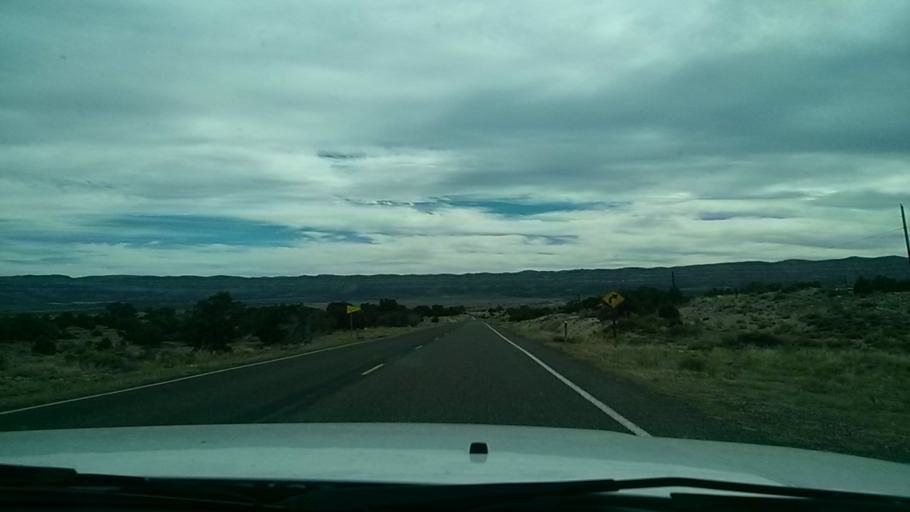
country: US
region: Utah
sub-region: Wayne County
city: Loa
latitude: 37.7306
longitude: -111.5182
